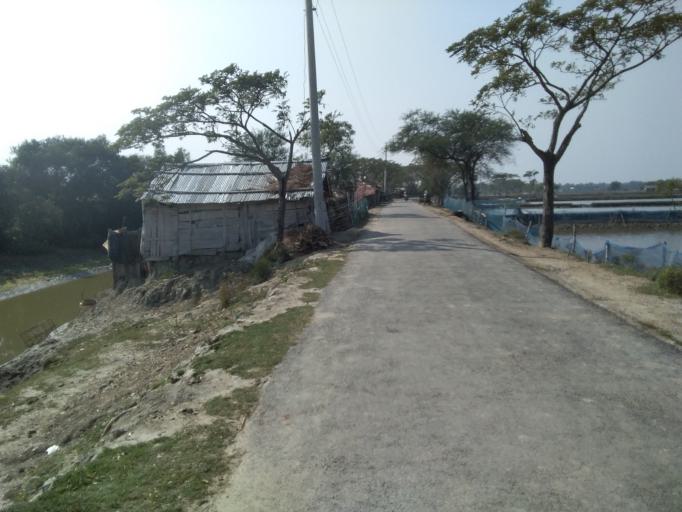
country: IN
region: West Bengal
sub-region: North 24 Parganas
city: Taki
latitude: 22.6347
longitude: 89.0100
